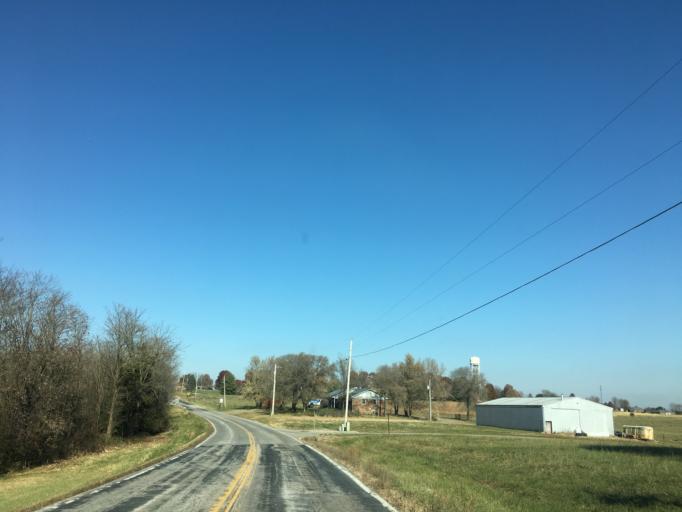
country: US
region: Missouri
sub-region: Cole County
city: Wardsville
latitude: 38.4797
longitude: -92.1765
